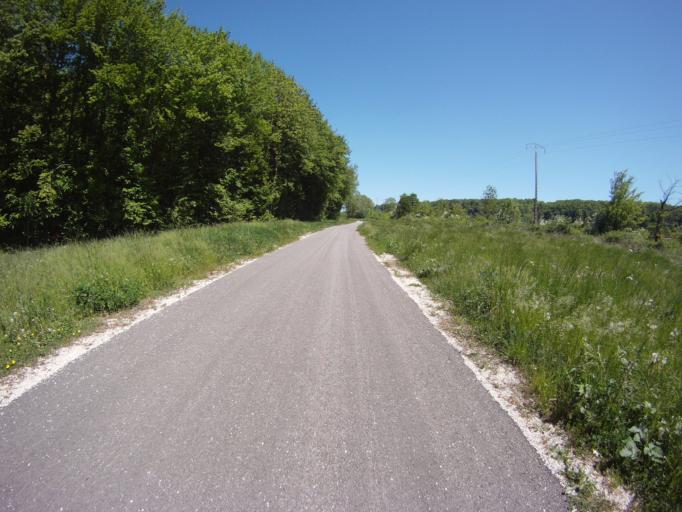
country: FR
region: Lorraine
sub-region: Departement de Meurthe-et-Moselle
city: Villey-Saint-Etienne
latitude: 48.7434
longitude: 6.0002
